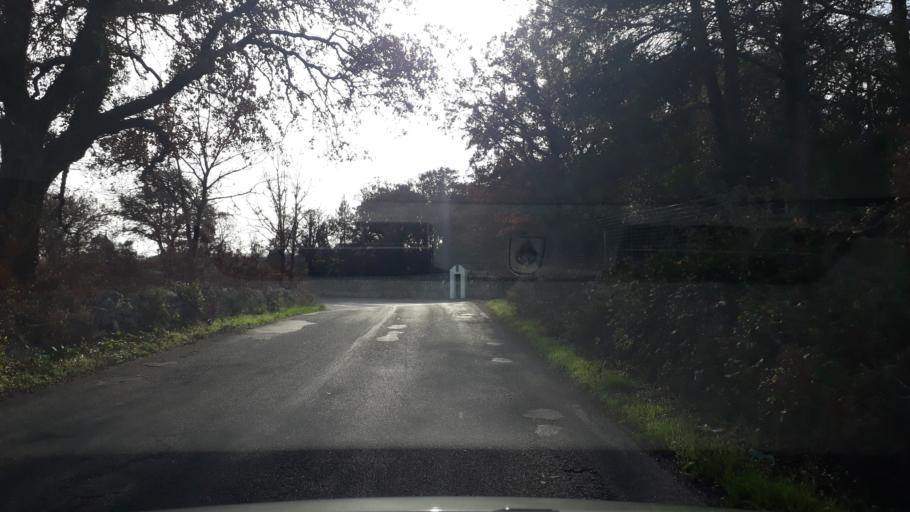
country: IT
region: Apulia
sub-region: Provincia di Taranto
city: Martina Franca
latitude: 40.6774
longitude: 17.3588
